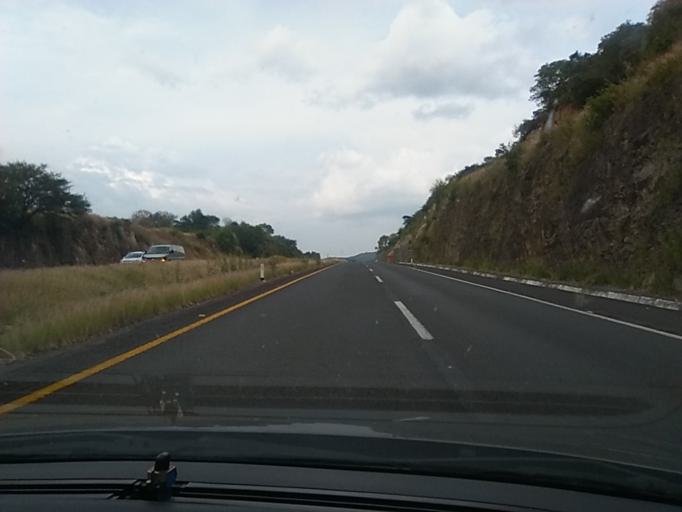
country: MX
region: Mexico
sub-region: Chapultepec
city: Chucandiro
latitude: 19.8850
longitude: -101.3349
